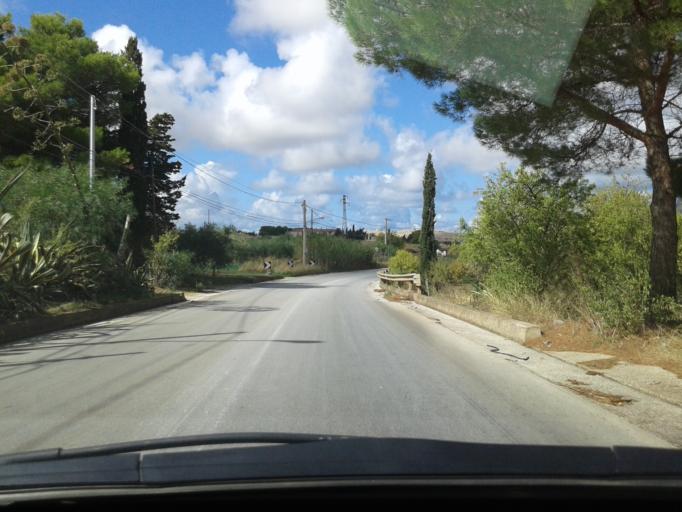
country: IT
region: Sicily
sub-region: Trapani
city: Castelluzzo
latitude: 38.0785
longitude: 12.7224
